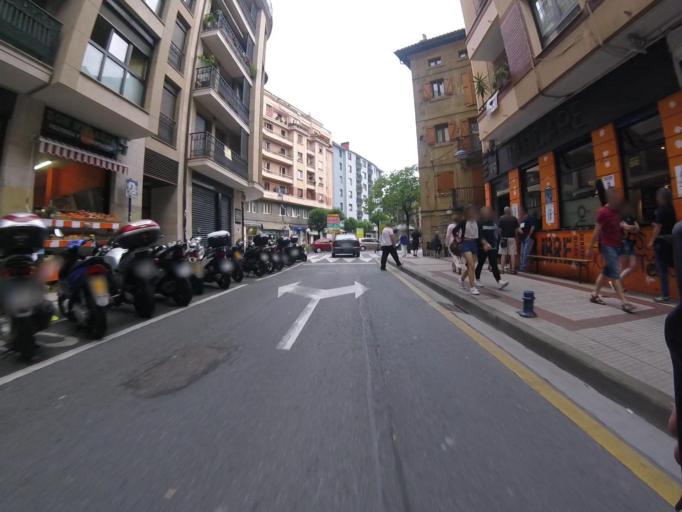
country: ES
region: Basque Country
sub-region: Provincia de Guipuzcoa
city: Errenteria
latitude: 43.3125
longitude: -1.9004
